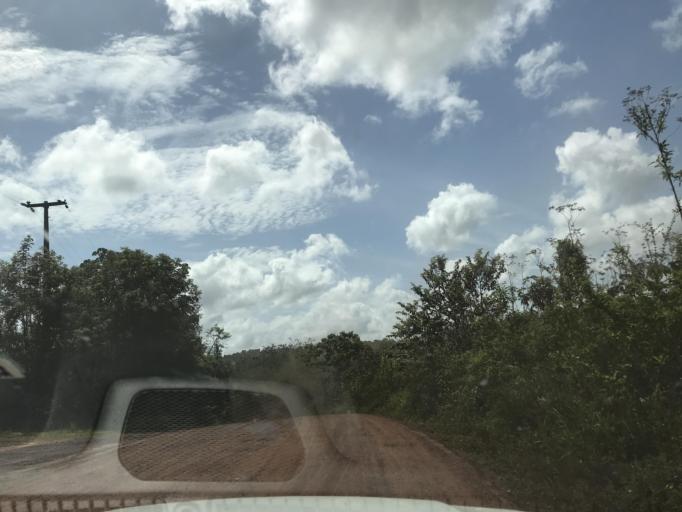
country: BR
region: Bahia
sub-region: Entre Rios
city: Entre Rios
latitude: -12.1649
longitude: -38.0746
